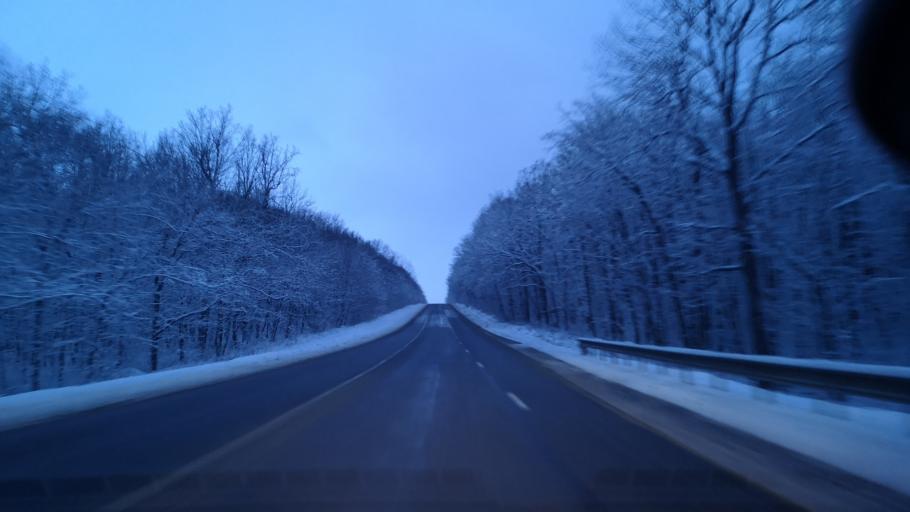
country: MD
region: Rezina
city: Rezina
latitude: 47.7270
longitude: 28.8622
